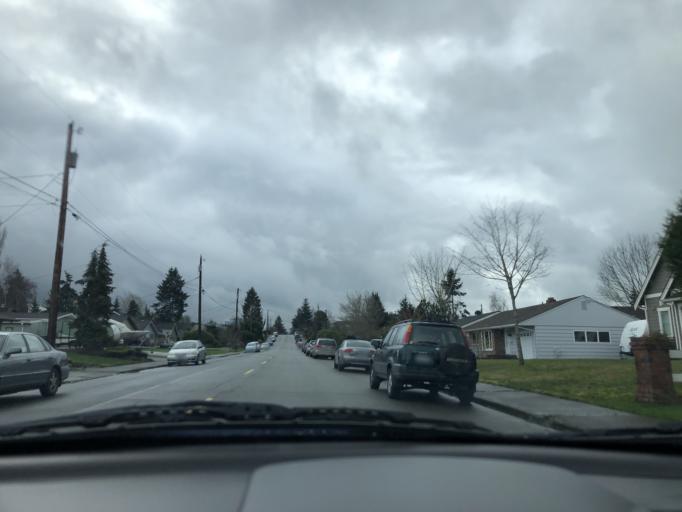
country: US
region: Washington
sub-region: Snohomish County
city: Everett
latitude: 48.0107
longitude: -122.2065
